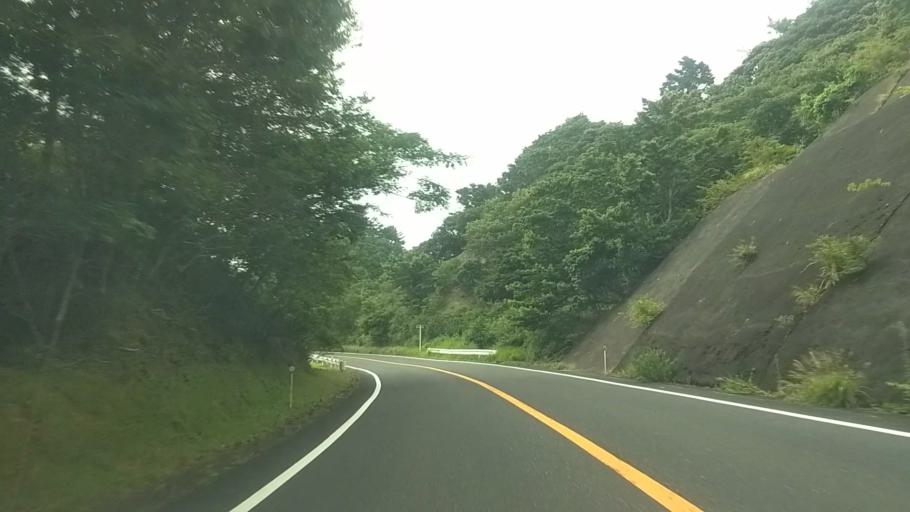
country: JP
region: Chiba
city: Kawaguchi
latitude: 35.2134
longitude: 140.0517
